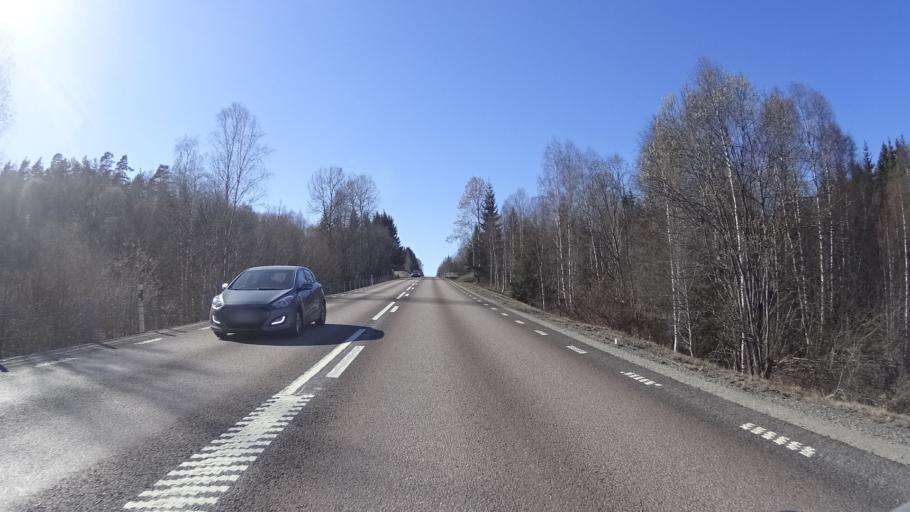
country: SE
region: Vaermland
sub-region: Arvika Kommun
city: Arvika
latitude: 59.6644
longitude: 12.8803
